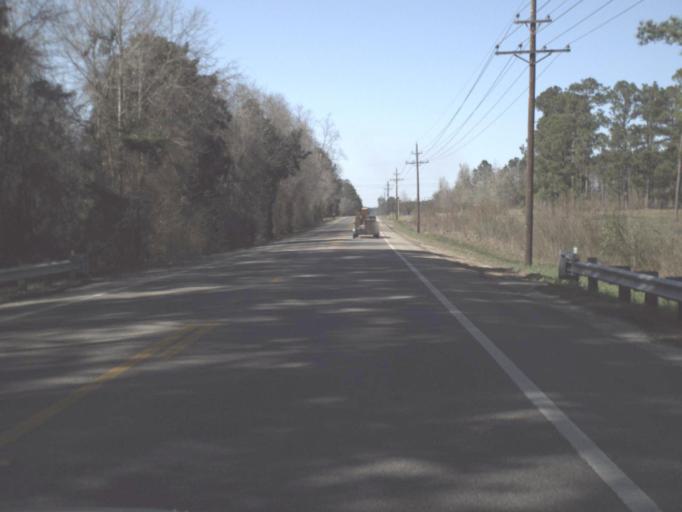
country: US
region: Florida
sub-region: Calhoun County
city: Blountstown
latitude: 30.5102
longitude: -85.1211
